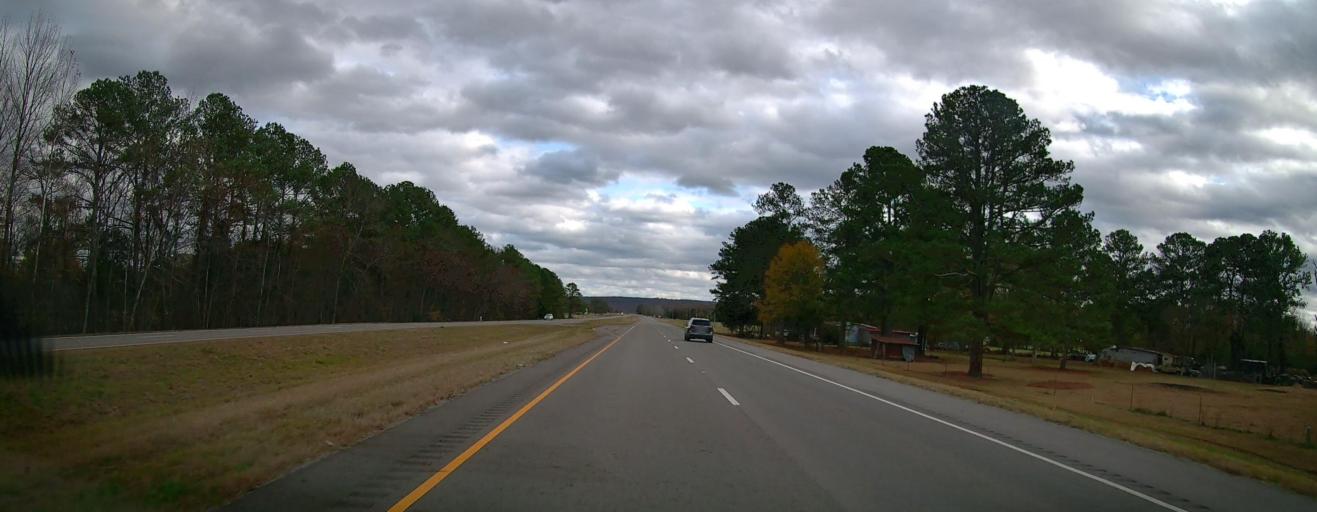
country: US
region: Alabama
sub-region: Morgan County
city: Danville
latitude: 34.3484
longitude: -87.0400
